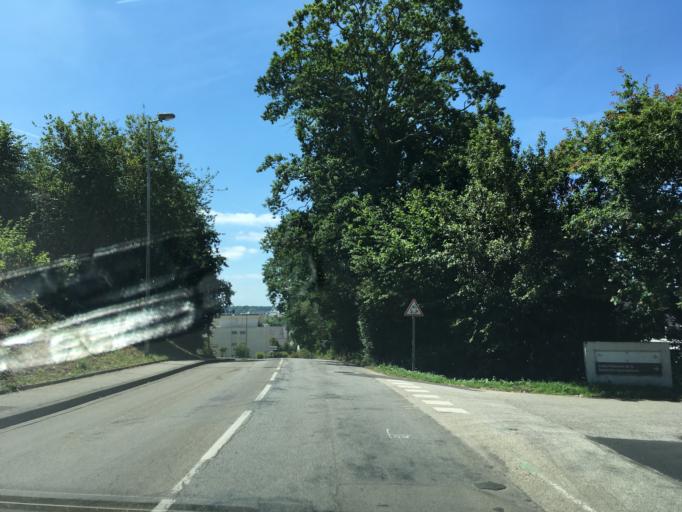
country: FR
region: Brittany
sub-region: Departement du Finistere
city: Quimper
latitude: 48.0075
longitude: -4.1075
